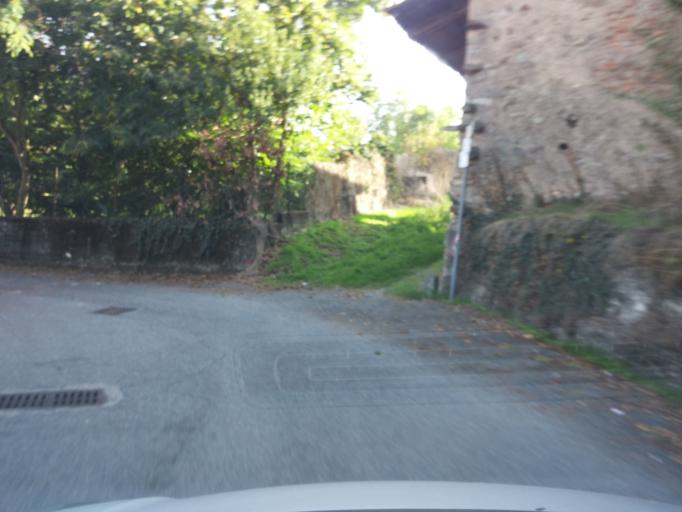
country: IT
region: Piedmont
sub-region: Provincia di Biella
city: Dorzano
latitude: 45.4255
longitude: 8.0950
